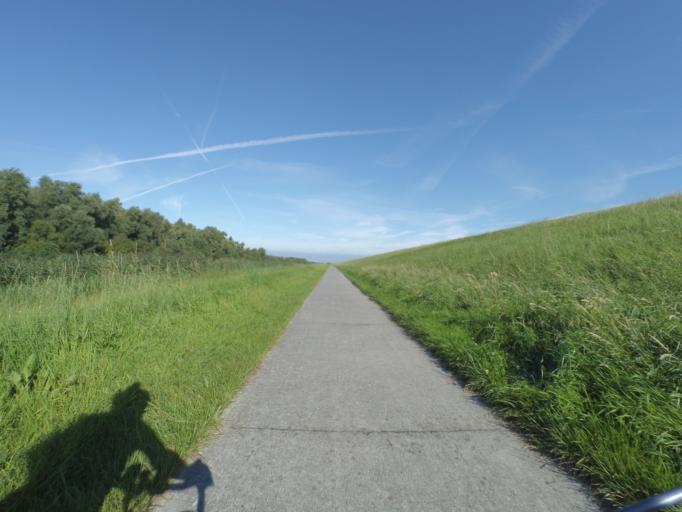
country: NL
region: Flevoland
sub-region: Gemeente Lelystad
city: Lelystad
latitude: 52.4136
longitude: 5.4852
